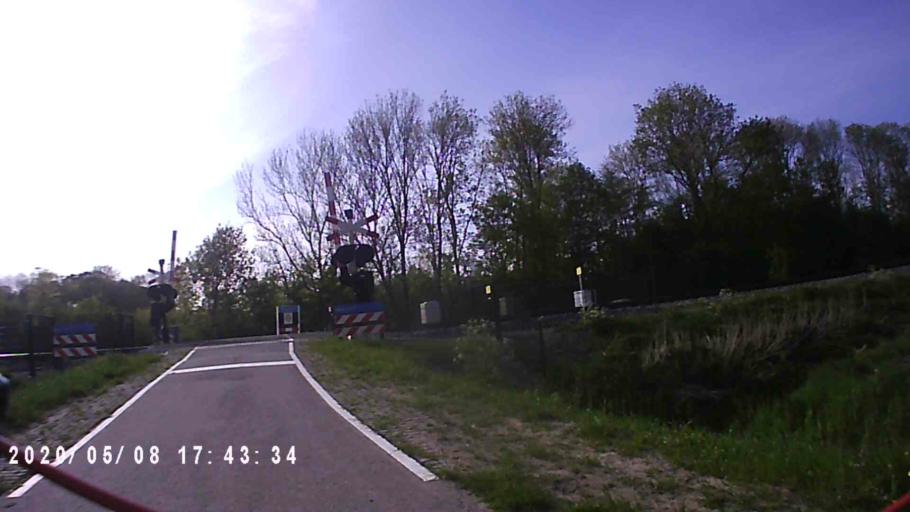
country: NL
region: Groningen
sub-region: Gemeente Winsum
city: Winsum
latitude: 53.3675
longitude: 6.5205
